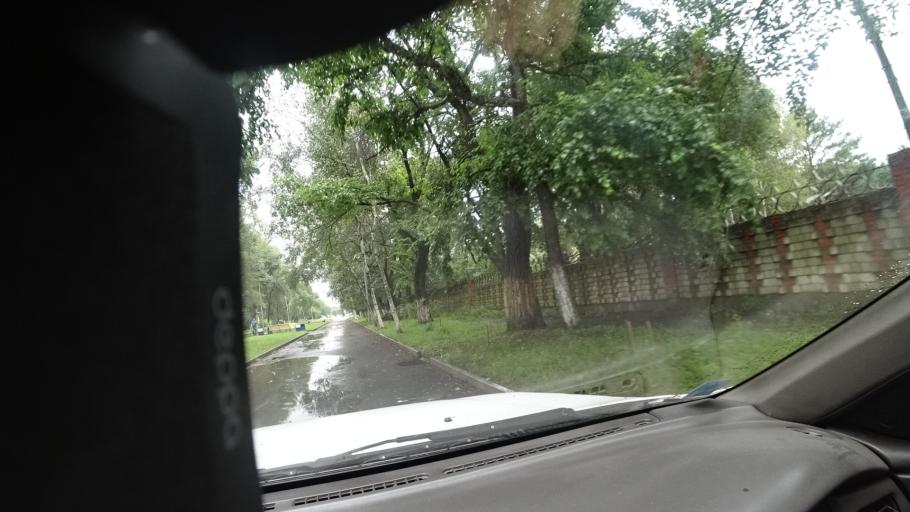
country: RU
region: Primorskiy
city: Dal'nerechensk
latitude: 45.9330
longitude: 133.7260
